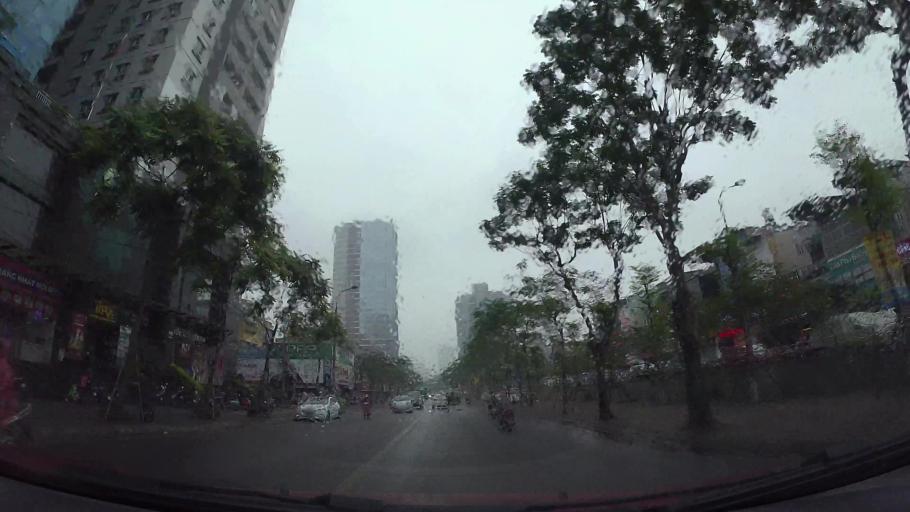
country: VN
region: Ha Noi
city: Dong Da
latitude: 21.0149
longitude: 105.8173
